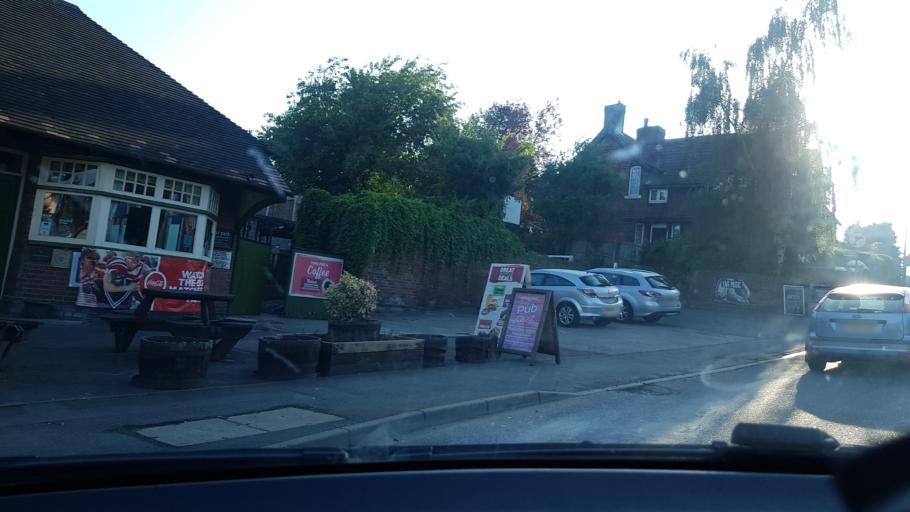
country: GB
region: England
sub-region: Derbyshire
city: Ilkeston
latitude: 52.9600
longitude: -1.3084
